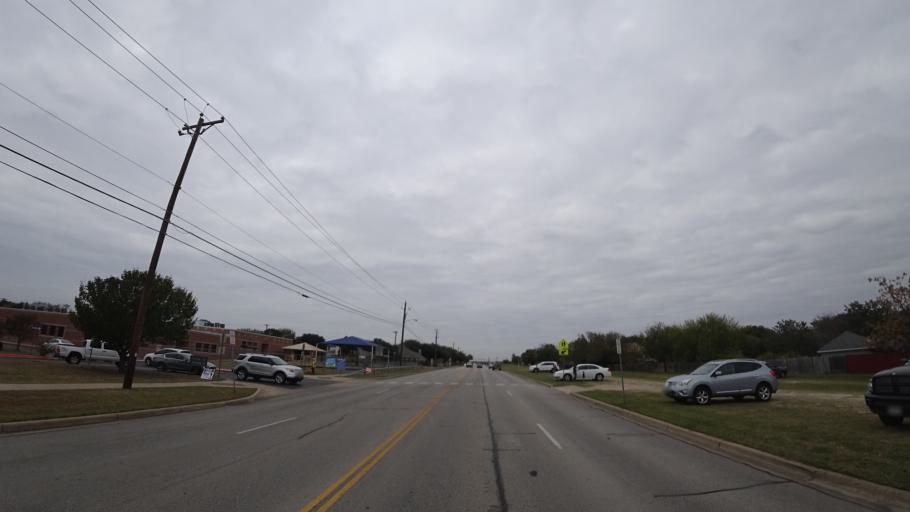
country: US
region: Texas
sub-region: Travis County
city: Pflugerville
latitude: 30.4521
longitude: -97.6172
